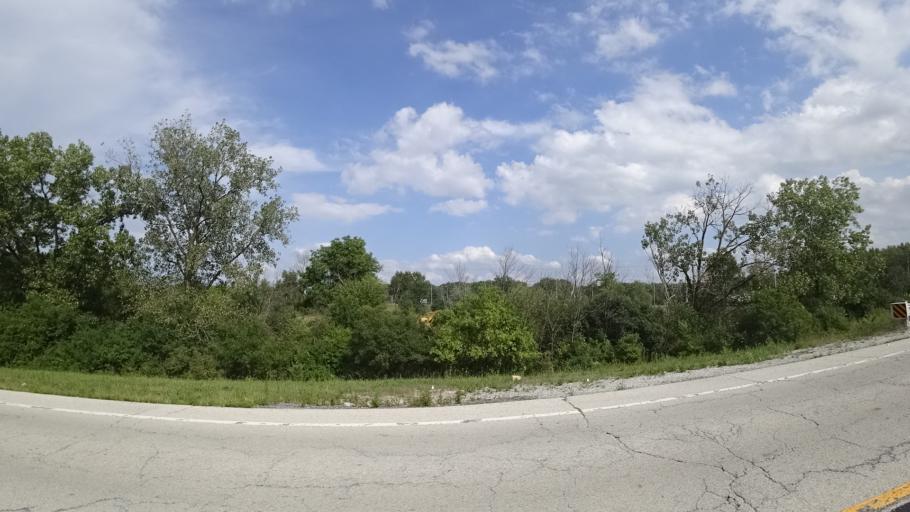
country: US
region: Illinois
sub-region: Cook County
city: Tinley Park
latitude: 41.5549
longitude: -87.7712
